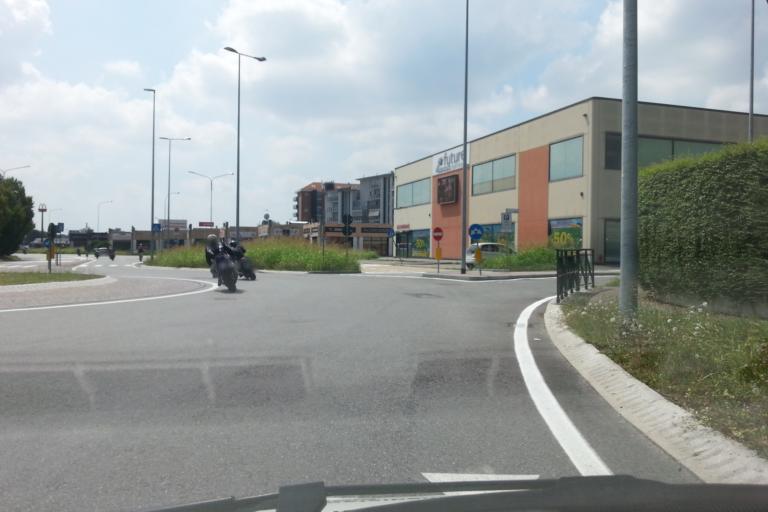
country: IT
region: Piedmont
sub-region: Provincia di Torino
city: Venaria Reale
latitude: 45.1151
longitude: 7.6439
